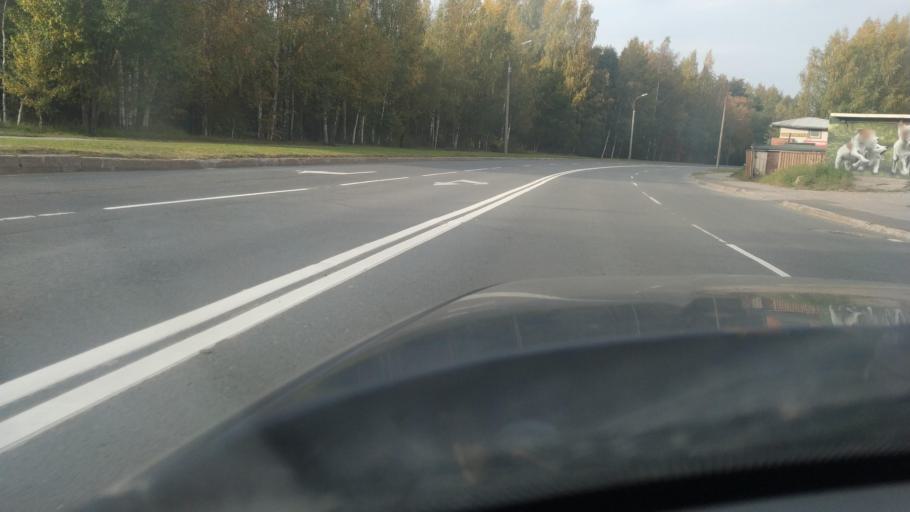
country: RU
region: Leningrad
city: Sosnovyy Bor
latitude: 59.8995
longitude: 29.1093
